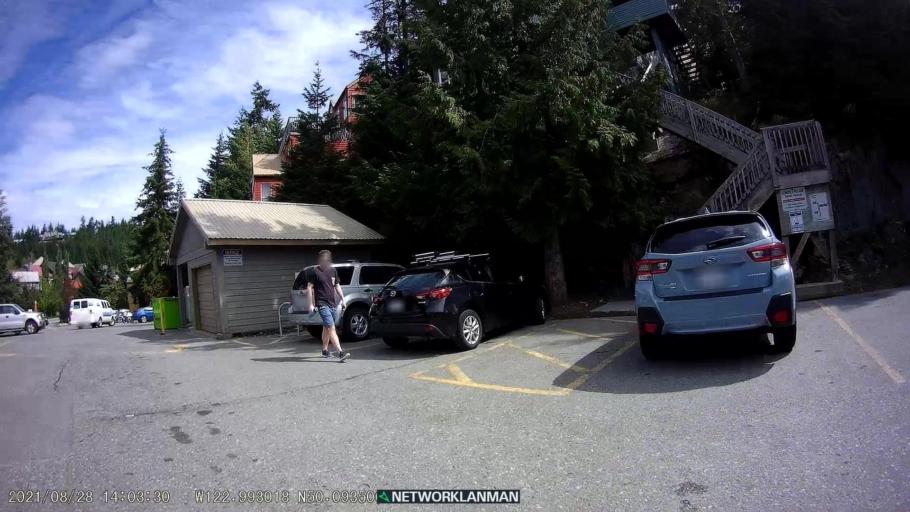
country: CA
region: British Columbia
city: Whistler
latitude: 50.0936
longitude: -122.9929
